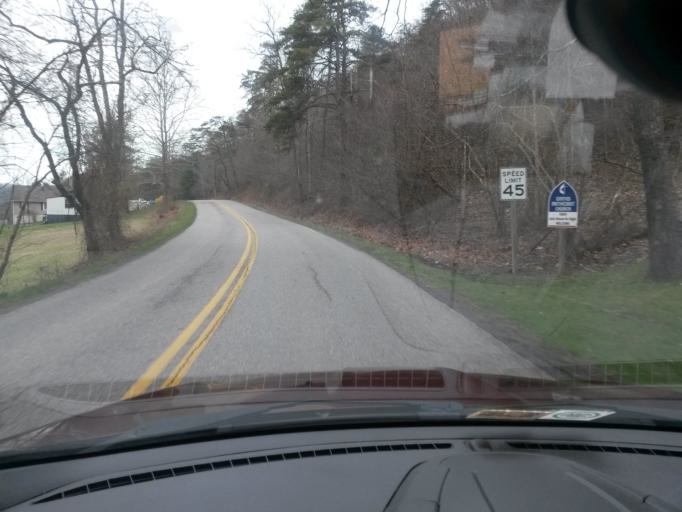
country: US
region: Virginia
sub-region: Bath County
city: Warm Springs
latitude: 38.0099
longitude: -79.8753
